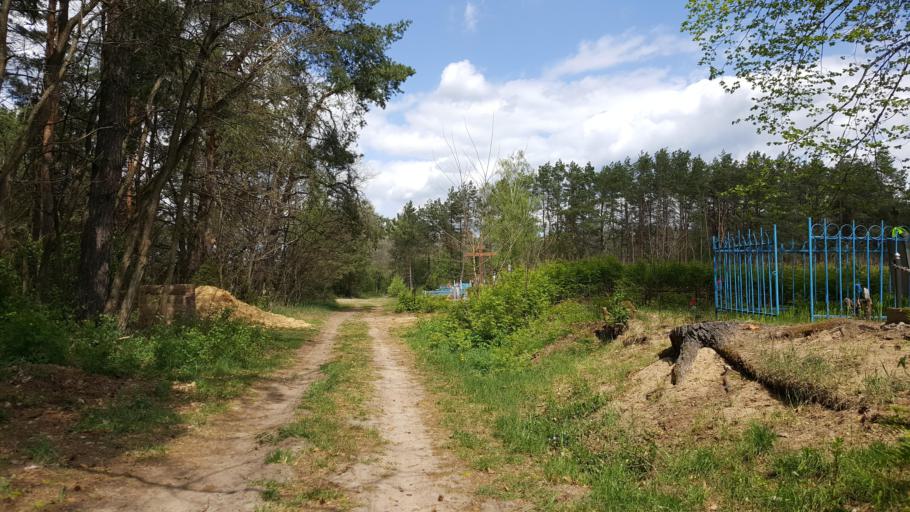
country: BY
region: Brest
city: Zhabinka
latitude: 52.4087
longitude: 24.0905
